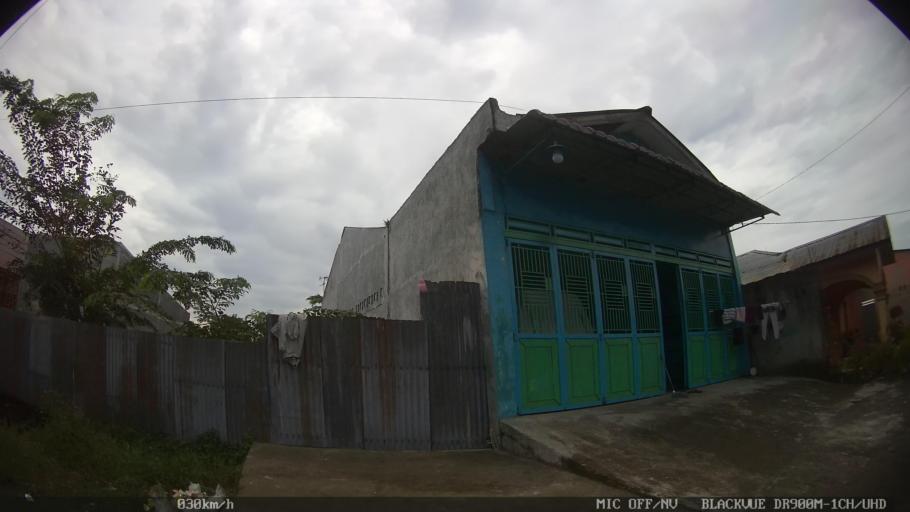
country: ID
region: North Sumatra
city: Sunggal
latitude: 3.5894
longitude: 98.5670
